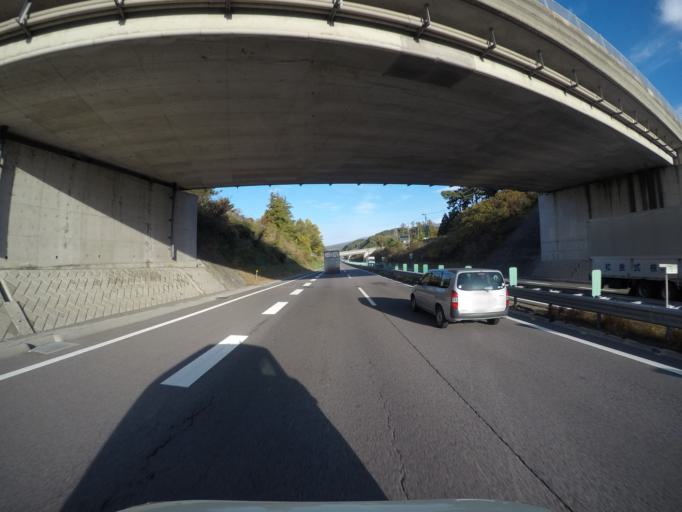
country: JP
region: Nagano
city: Komoro
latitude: 36.3327
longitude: 138.4467
